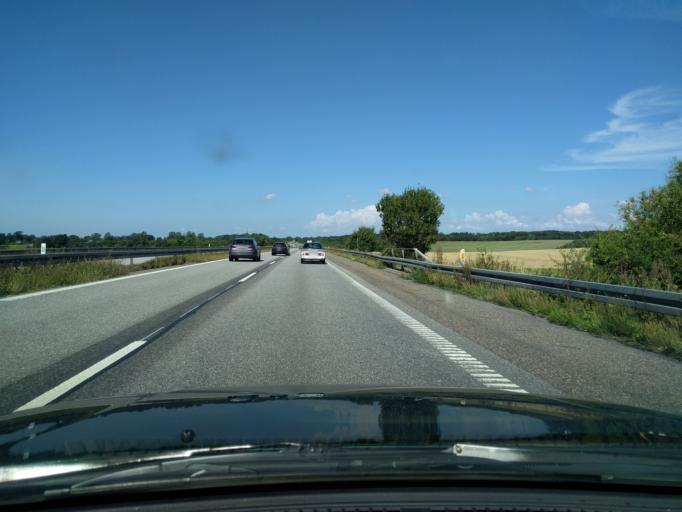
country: DK
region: Zealand
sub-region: Vordingborg Kommune
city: Orslev
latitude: 55.0683
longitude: 11.9642
